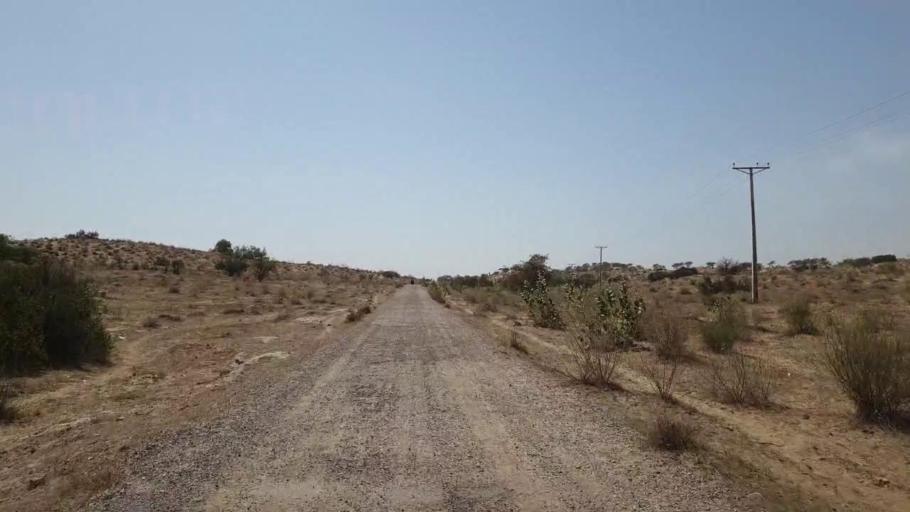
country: PK
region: Sindh
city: Umarkot
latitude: 25.2154
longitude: 69.9364
